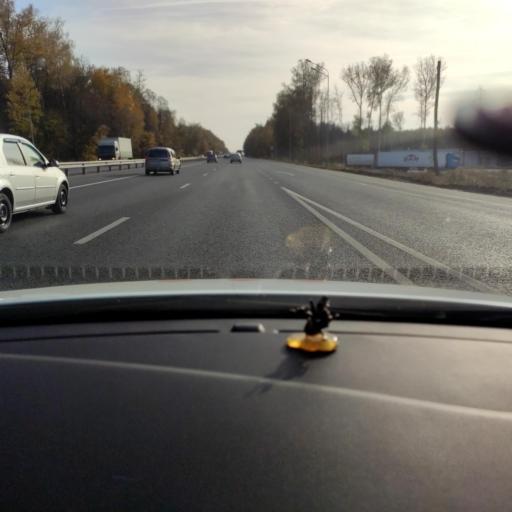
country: RU
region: Tatarstan
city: Osinovo
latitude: 55.8481
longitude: 48.8528
